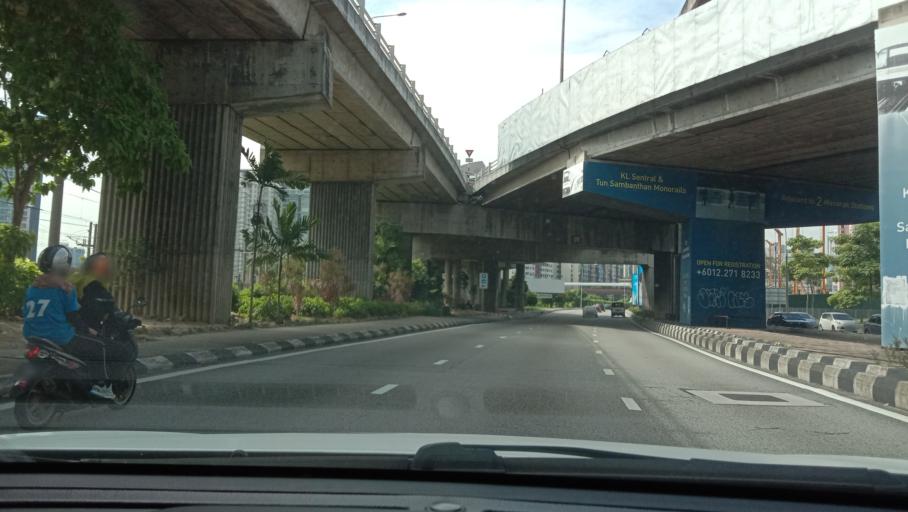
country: MY
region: Kuala Lumpur
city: Kuala Lumpur
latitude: 3.1254
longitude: 101.6781
